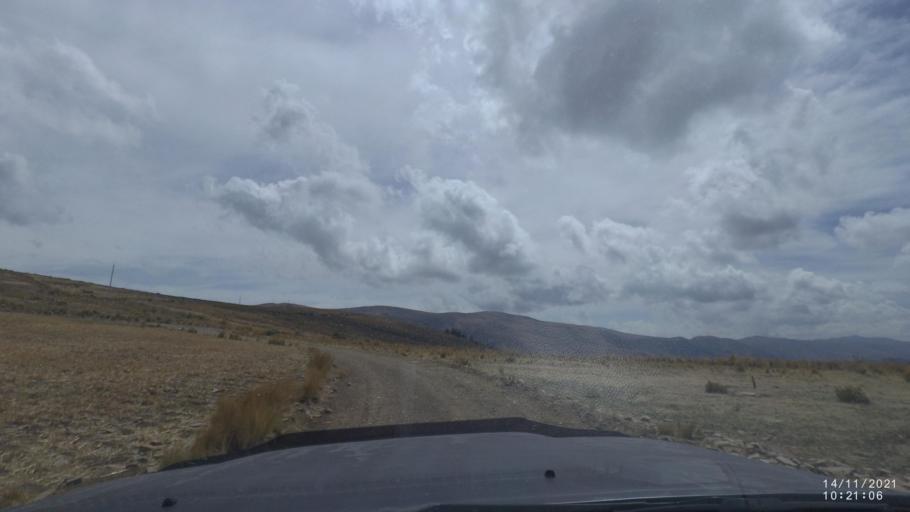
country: BO
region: Cochabamba
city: Cochabamba
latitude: -17.3337
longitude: -66.0801
